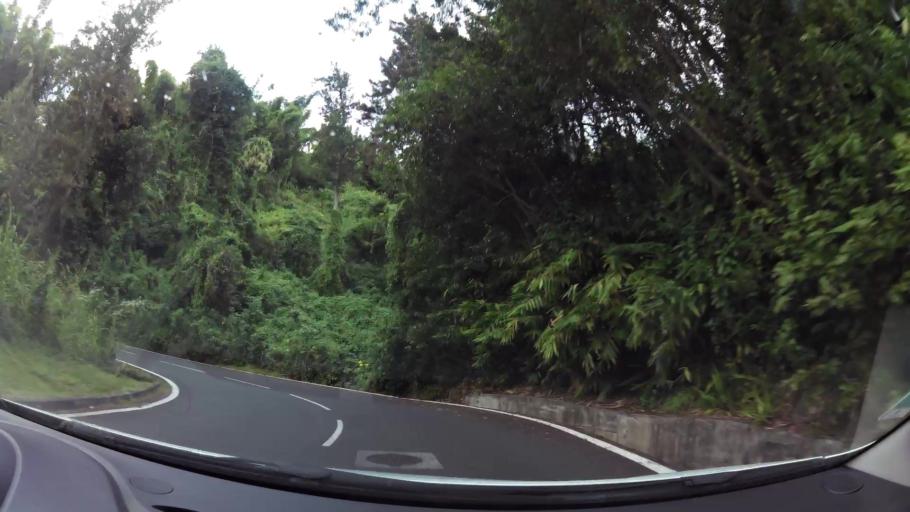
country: RE
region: Reunion
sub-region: Reunion
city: Saint-Denis
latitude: -20.9062
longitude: 55.4421
